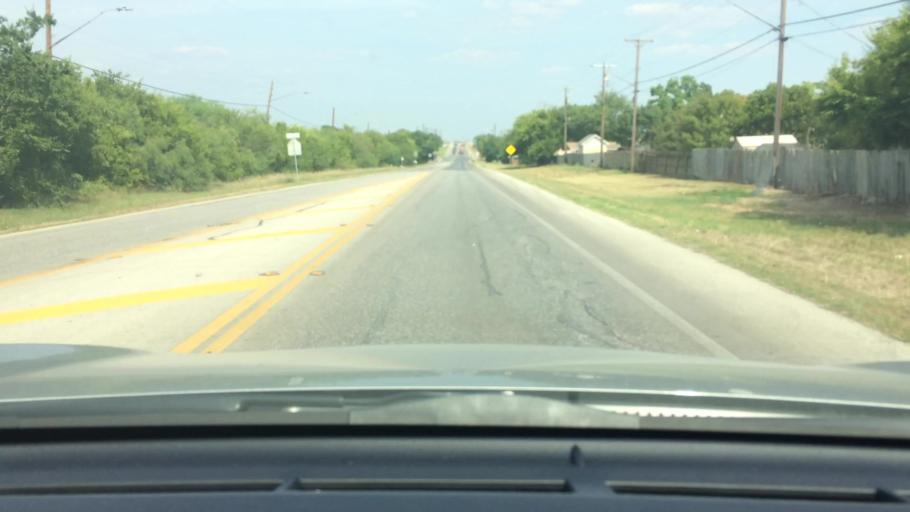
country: US
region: Texas
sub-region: Bexar County
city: China Grove
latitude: 29.3276
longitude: -98.4366
